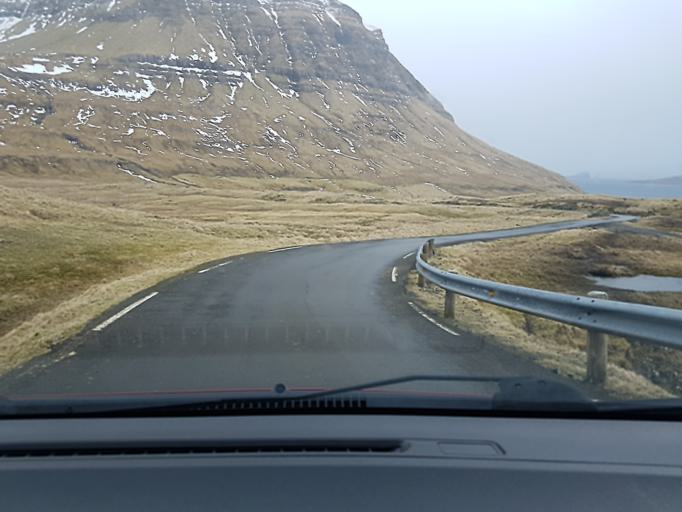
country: FO
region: Streymoy
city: Kollafjordhur
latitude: 62.0444
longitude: -6.9267
